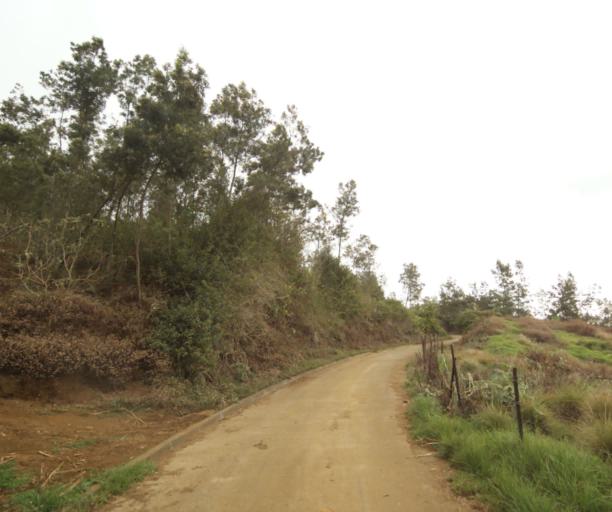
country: RE
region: Reunion
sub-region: Reunion
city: Saint-Paul
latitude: -21.0134
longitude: 55.3580
